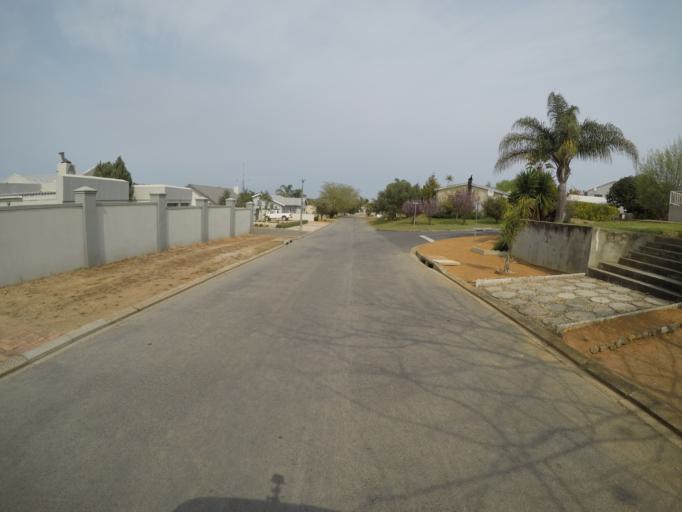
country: ZA
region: Western Cape
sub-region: West Coast District Municipality
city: Malmesbury
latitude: -33.4610
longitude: 18.7413
